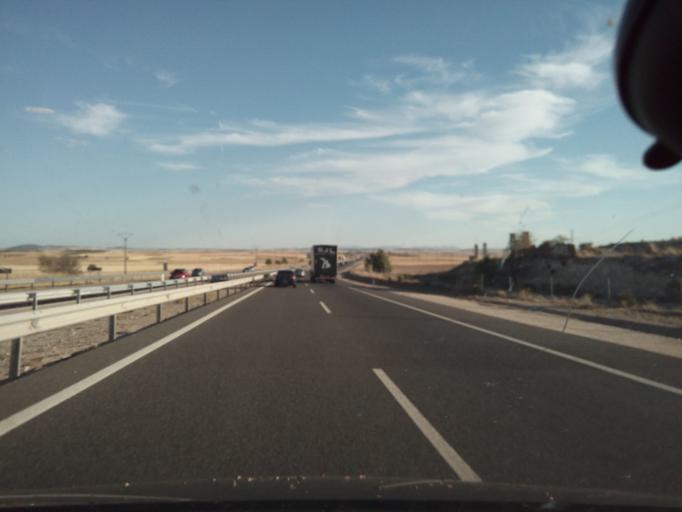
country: ES
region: Castille-La Mancha
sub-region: Province of Toledo
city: Tembleque
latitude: 39.7617
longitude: -3.4814
